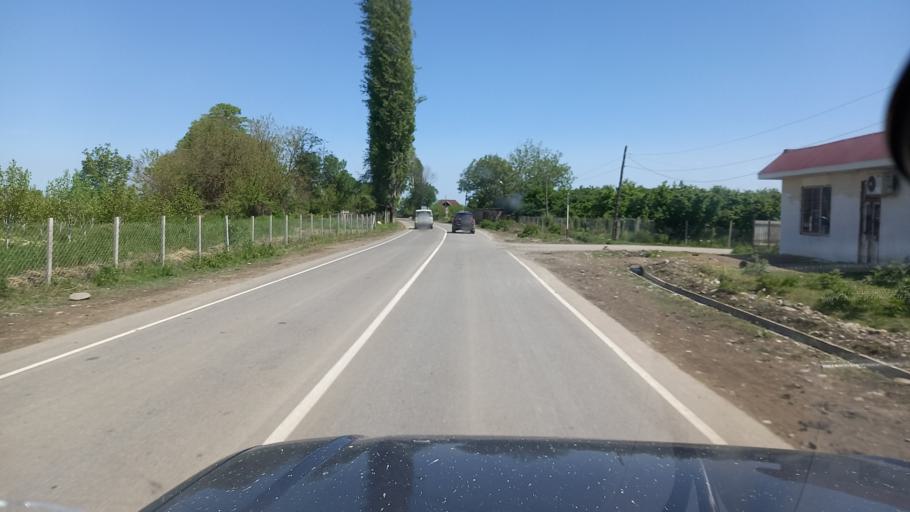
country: RU
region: Dagestan
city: Samur
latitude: 41.7913
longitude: 48.4953
